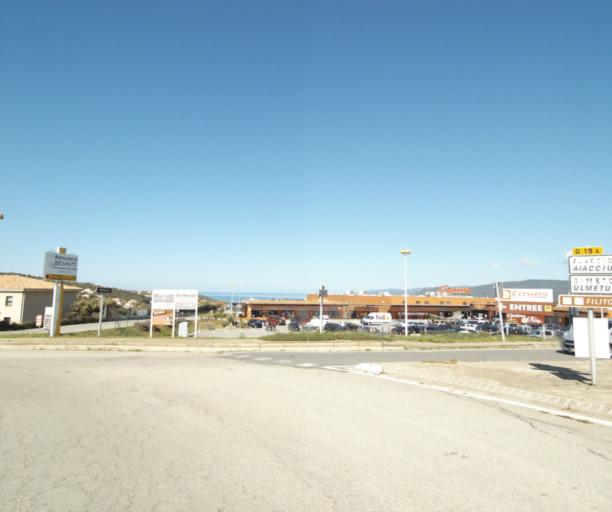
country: FR
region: Corsica
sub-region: Departement de la Corse-du-Sud
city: Propriano
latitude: 41.6719
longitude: 8.9185
